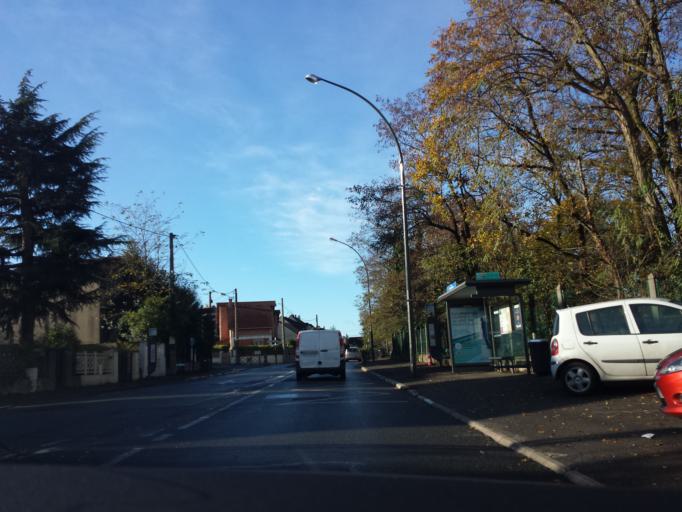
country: FR
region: Ile-de-France
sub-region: Departement de l'Essonne
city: Palaiseau
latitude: 48.7314
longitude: 2.2541
